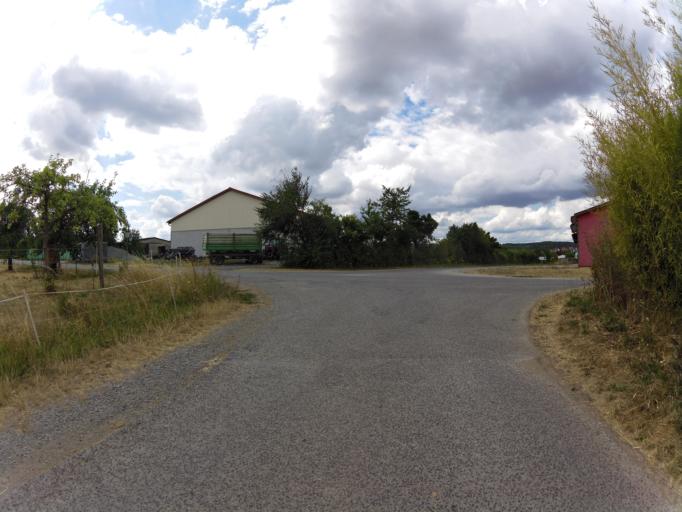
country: DE
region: Bavaria
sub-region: Regierungsbezirk Unterfranken
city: Zellingen
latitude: 49.8885
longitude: 9.8144
